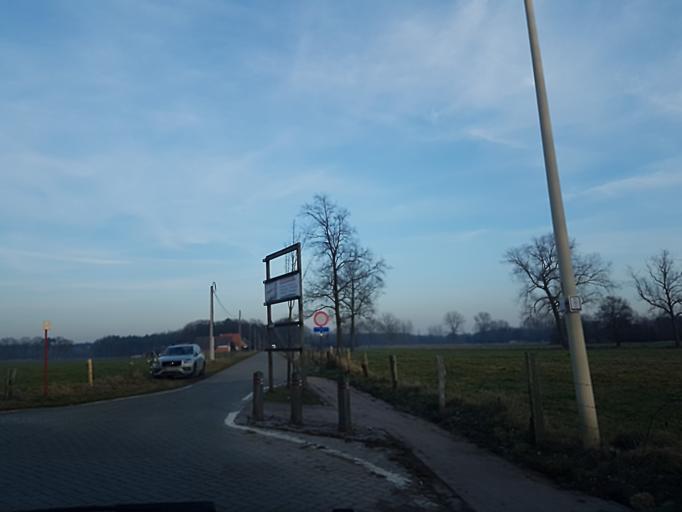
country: BE
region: Flanders
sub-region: Provincie Antwerpen
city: Zandhoven
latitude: 51.2484
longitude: 4.6470
